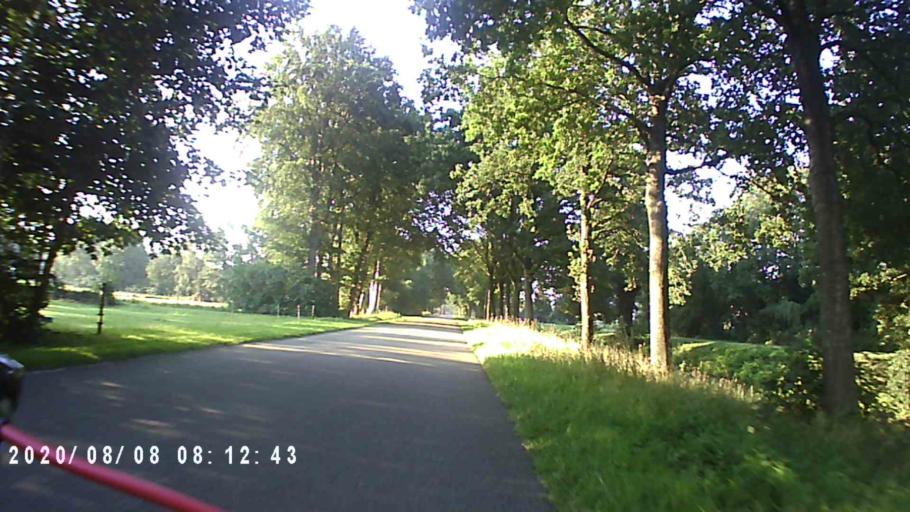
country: NL
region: Groningen
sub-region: Gemeente Leek
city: Leek
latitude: 53.1028
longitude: 6.3395
